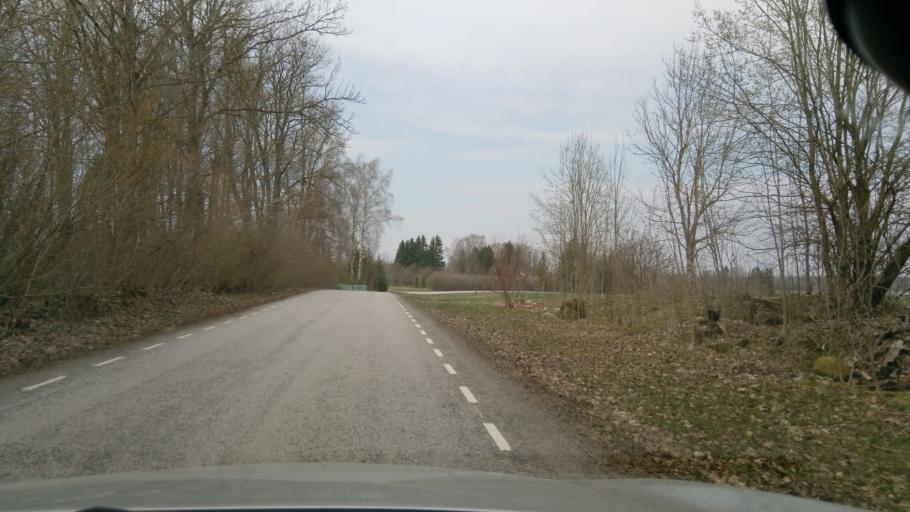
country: EE
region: Jaervamaa
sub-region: Tueri vald
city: Sarevere
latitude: 58.7849
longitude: 25.4745
